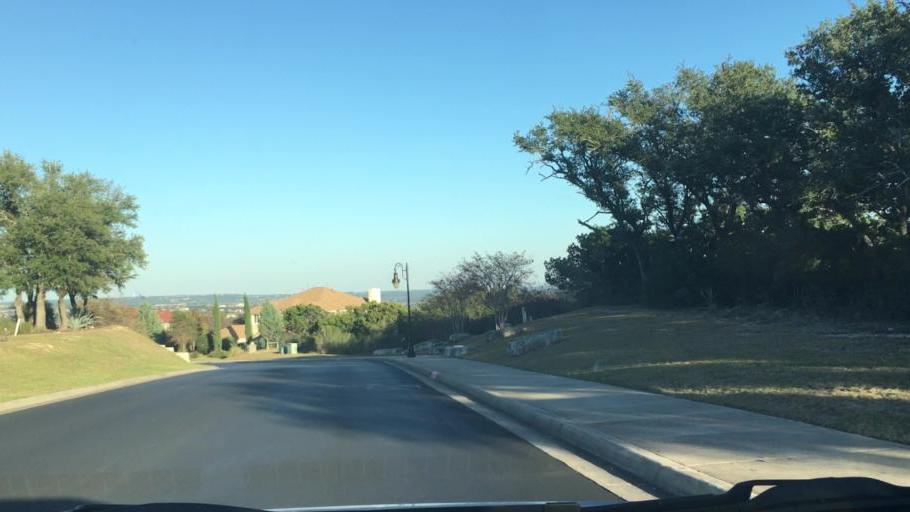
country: US
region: Texas
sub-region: Travis County
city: Bee Cave
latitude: 30.3313
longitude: -97.9602
